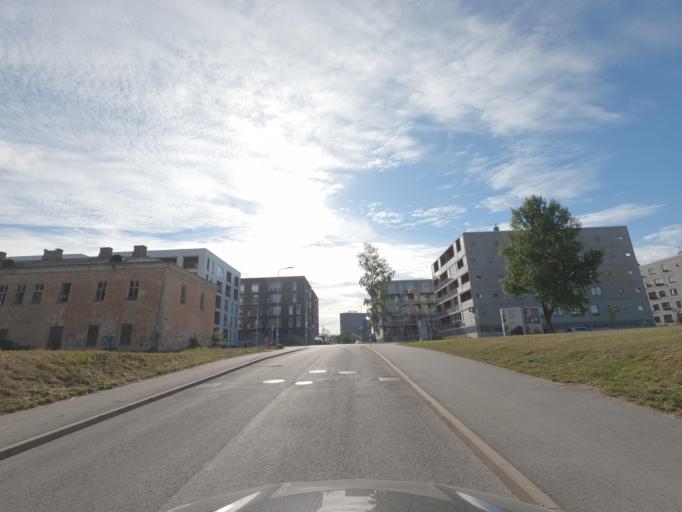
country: EE
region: Harju
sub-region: Tallinna linn
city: Tallinn
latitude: 59.4066
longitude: 24.7242
